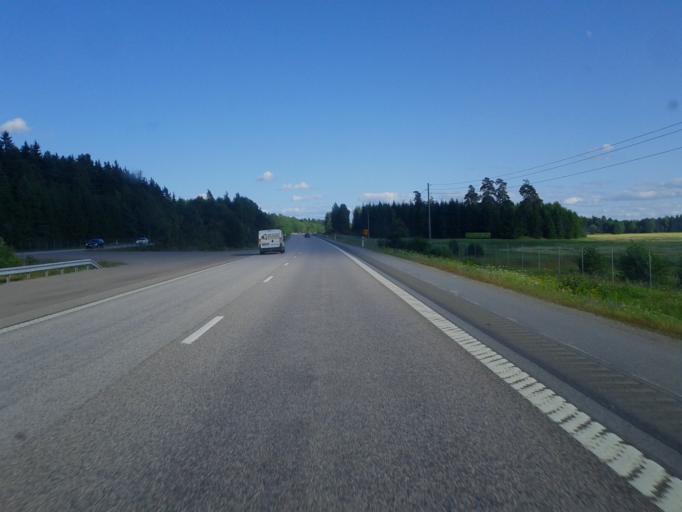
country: SE
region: Uppsala
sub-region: Habo Kommun
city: Balsta
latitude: 59.5555
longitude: 17.5824
